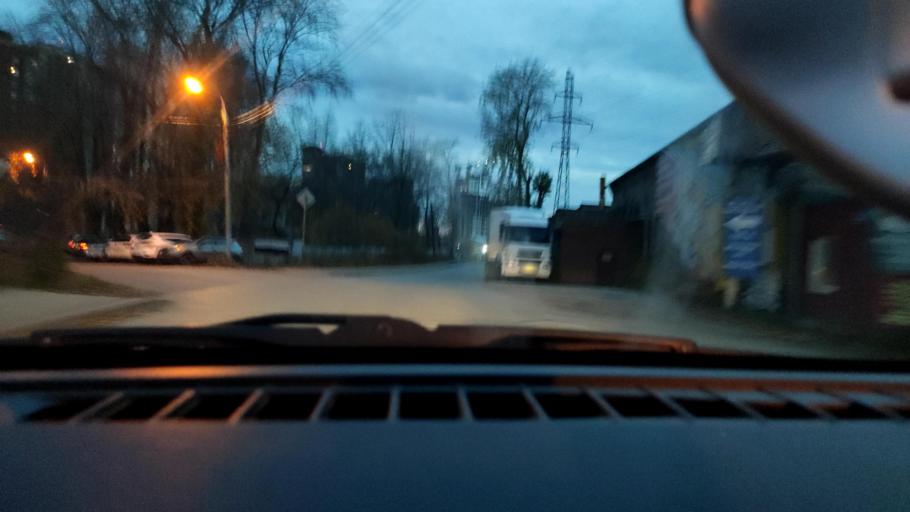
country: RU
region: Perm
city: Kondratovo
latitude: 58.0000
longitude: 56.1654
